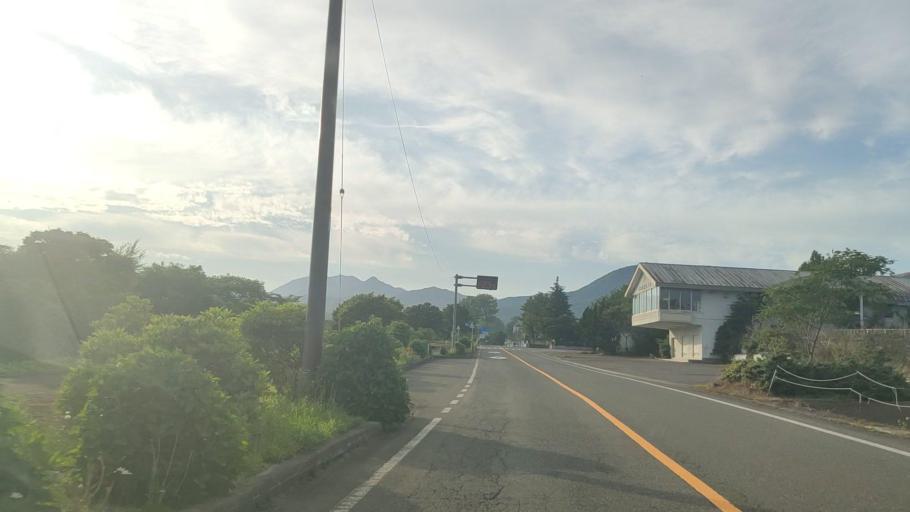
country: JP
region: Tottori
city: Kurayoshi
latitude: 35.2959
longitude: 133.6342
